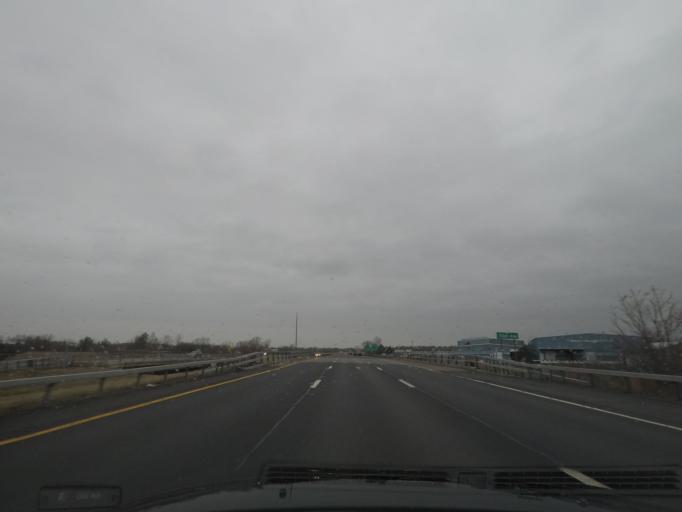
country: US
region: New York
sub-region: Rensselaer County
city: Hampton Manor
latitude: 42.6437
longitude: -73.7102
